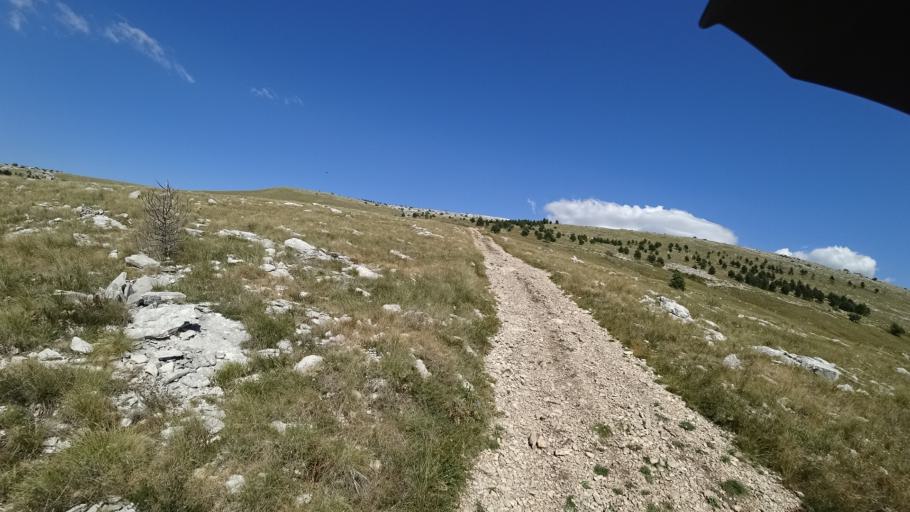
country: HR
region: Splitsko-Dalmatinska
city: Hrvace
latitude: 43.8650
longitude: 16.6446
